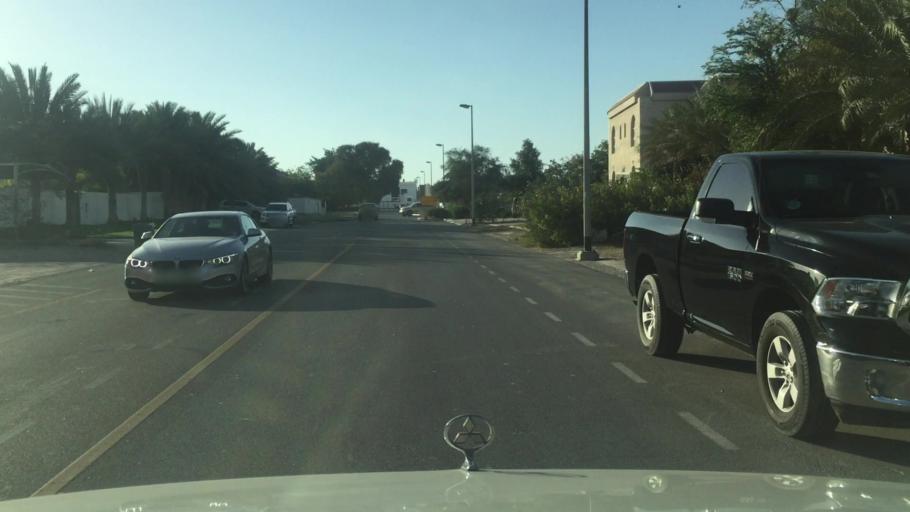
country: AE
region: Dubai
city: Dubai
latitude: 25.1617
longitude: 55.2291
